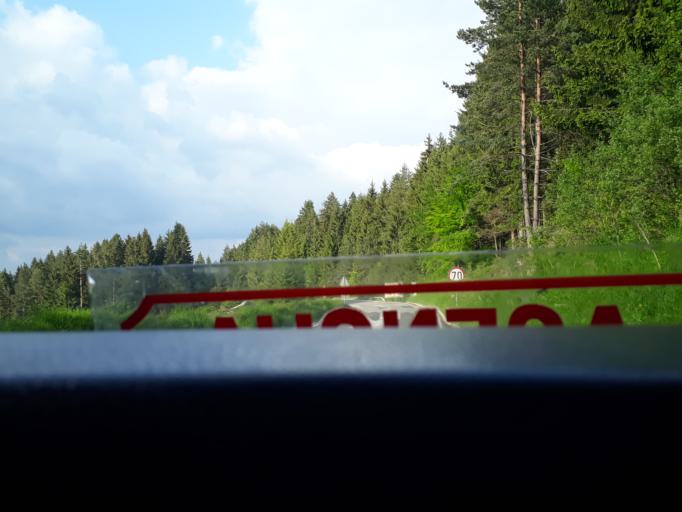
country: BA
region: Federation of Bosnia and Herzegovina
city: Olovo
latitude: 44.0620
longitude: 18.4826
